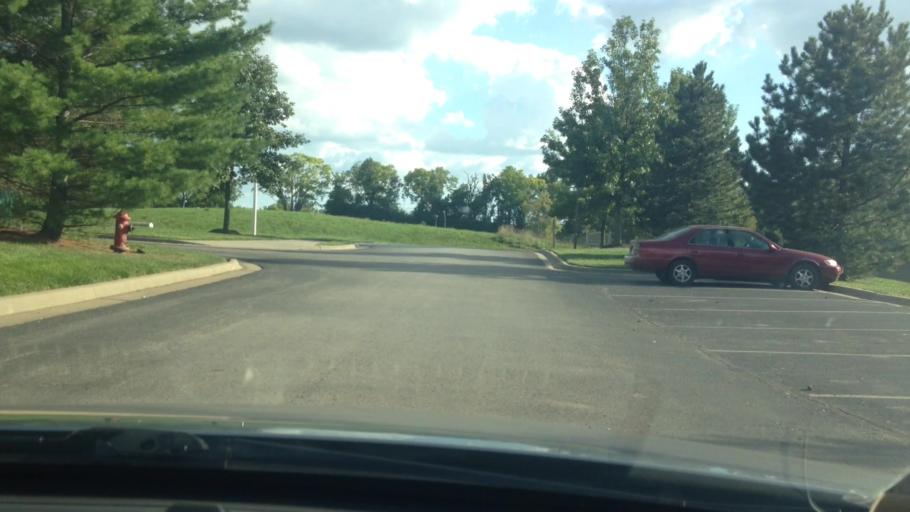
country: US
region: Missouri
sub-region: Clay County
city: Claycomo
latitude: 39.1721
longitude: -94.5049
